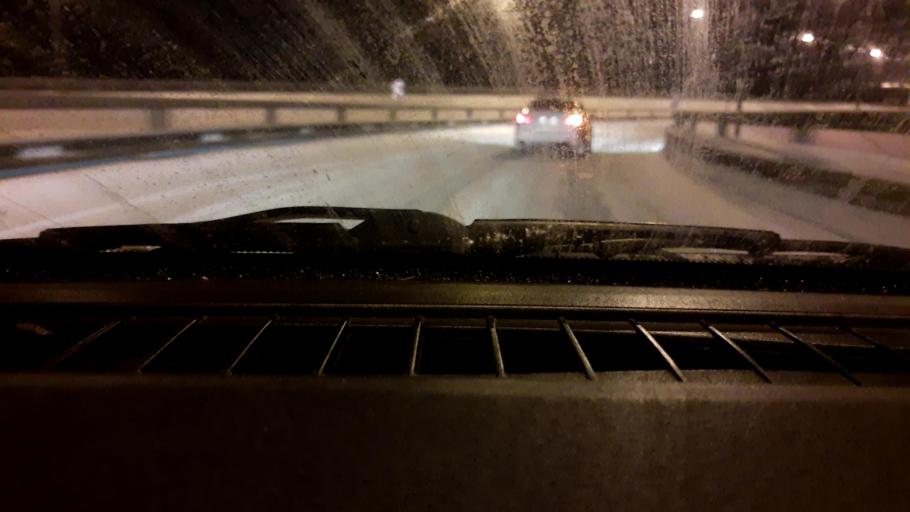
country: RU
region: Moskovskaya
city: Demikhovo
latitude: 55.8574
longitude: 38.8906
